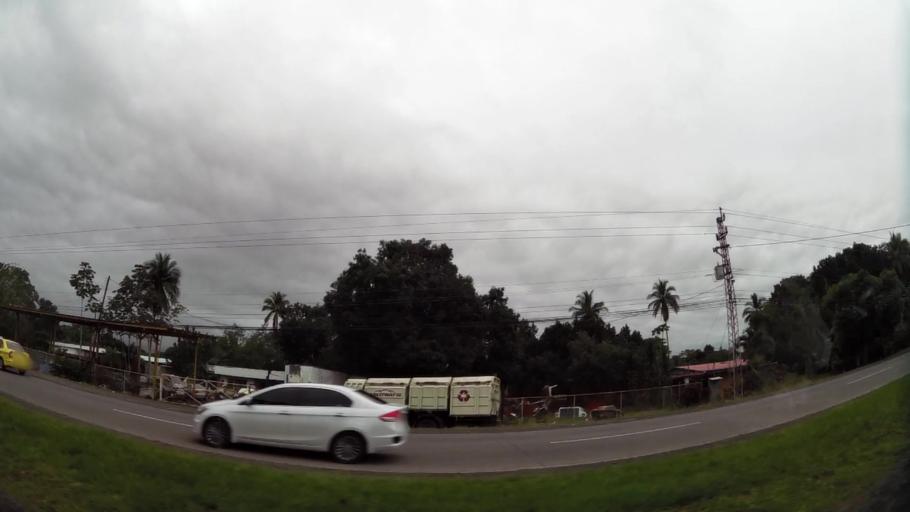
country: PA
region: Chiriqui
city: Tijera
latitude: 8.4698
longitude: -82.5336
